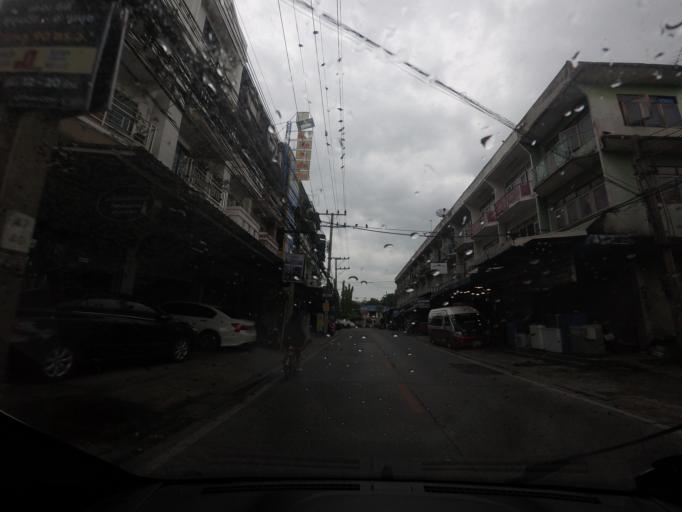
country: TH
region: Bangkok
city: Watthana
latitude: 13.7277
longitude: 100.6110
